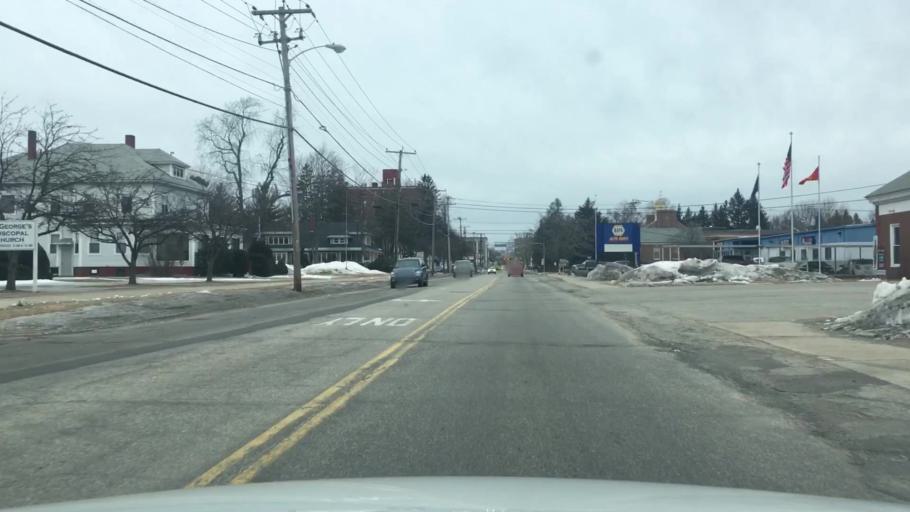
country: US
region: Maine
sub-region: York County
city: Sanford (historical)
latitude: 43.4350
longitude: -70.7722
